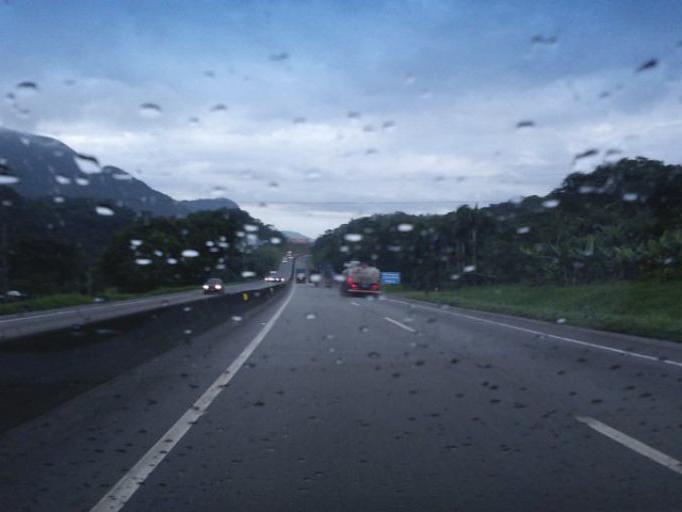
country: BR
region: Parana
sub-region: Guaratuba
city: Guaratuba
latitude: -25.9500
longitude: -48.9056
